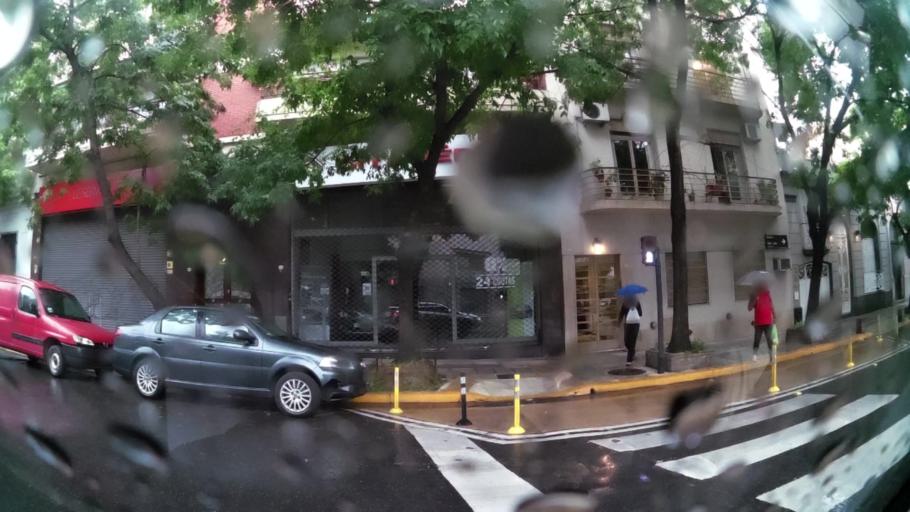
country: AR
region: Buenos Aires F.D.
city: Buenos Aires
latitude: -34.6290
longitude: -58.3721
